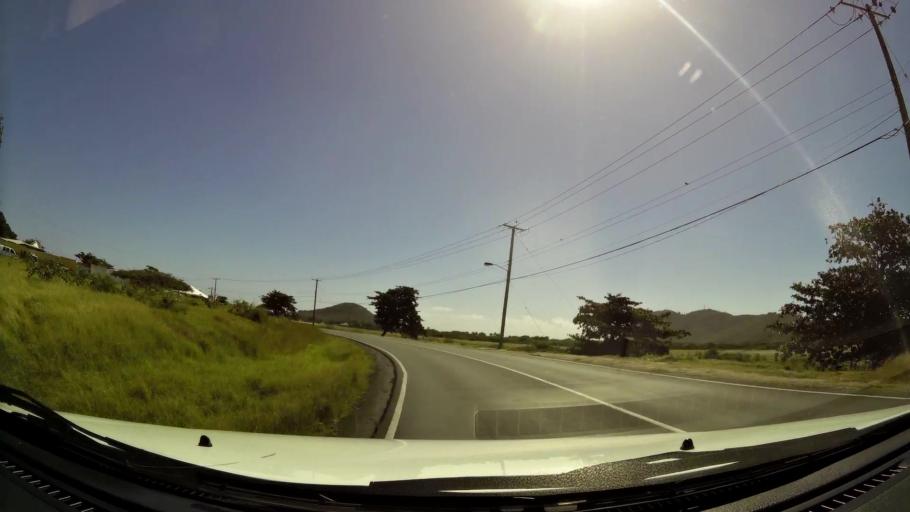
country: LC
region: Vieux-Fort
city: Vieux Fort
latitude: 13.7359
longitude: -60.9451
